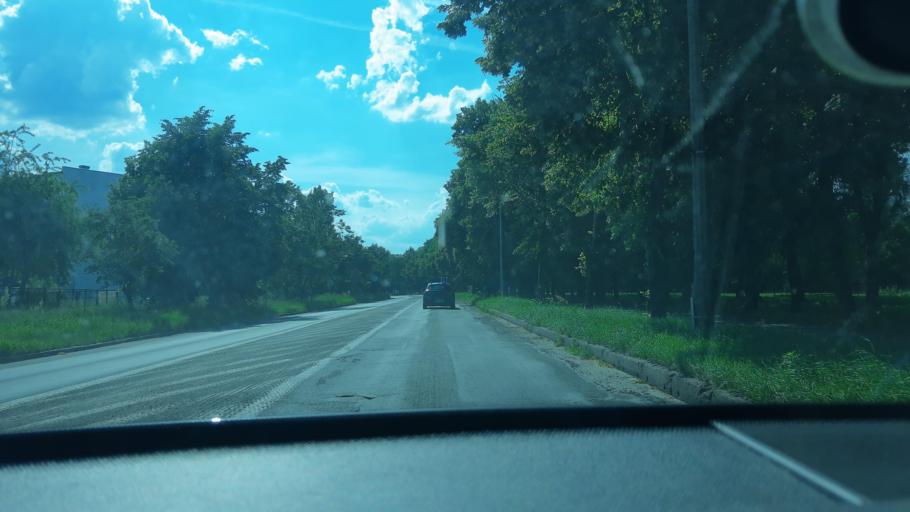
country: PL
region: Lodz Voivodeship
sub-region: Powiat zdunskowolski
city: Zdunska Wola
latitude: 51.6077
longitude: 18.9275
